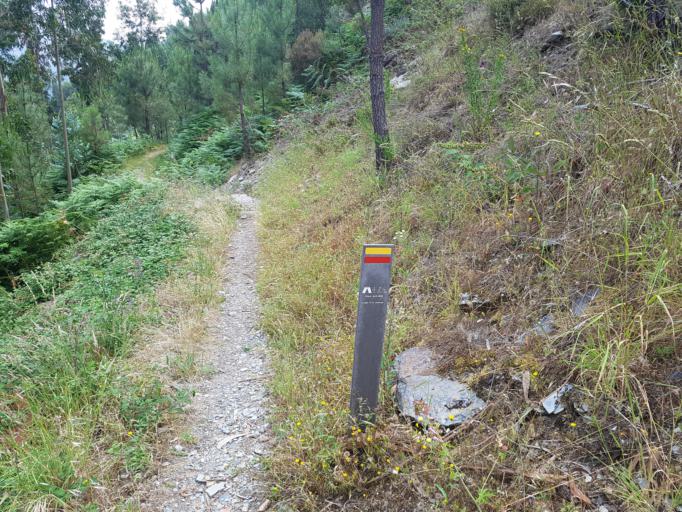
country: PT
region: Coimbra
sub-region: Oliveira do Hospital
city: Oliveira do Hospital
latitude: 40.2326
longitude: -7.8243
